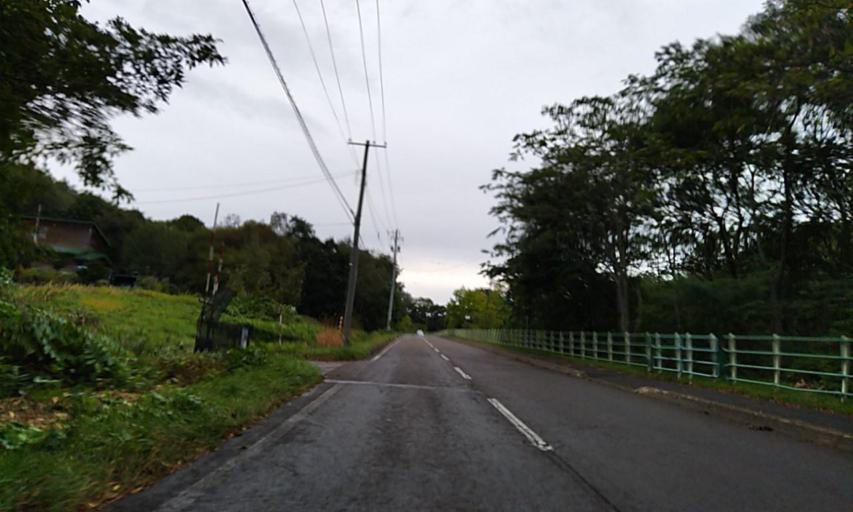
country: JP
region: Hokkaido
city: Abashiri
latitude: 44.0002
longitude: 144.2293
